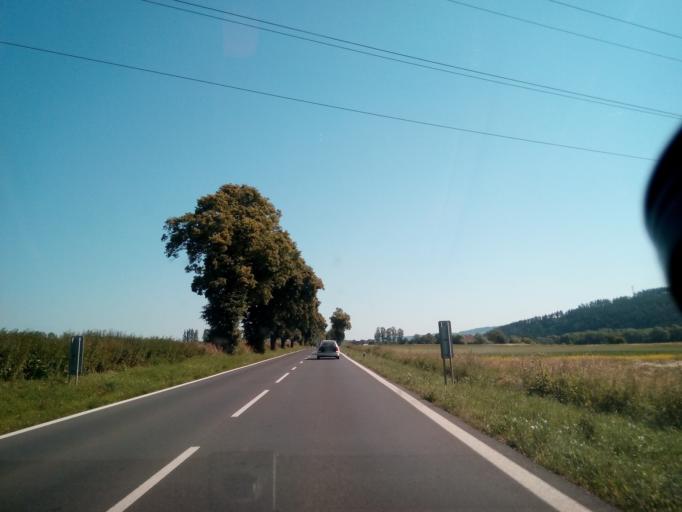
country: SK
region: Presovsky
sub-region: Okres Presov
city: Kezmarok
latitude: 49.1554
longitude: 20.4367
